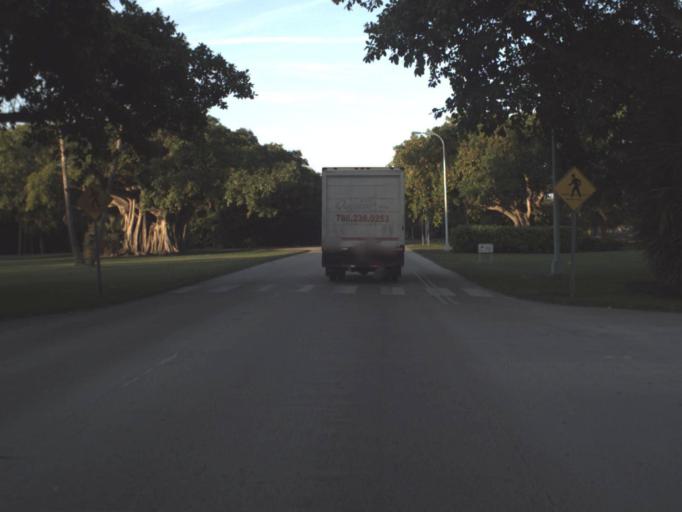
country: US
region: Florida
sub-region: Miami-Dade County
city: Key Biscayne
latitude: 25.7097
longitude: -80.1564
